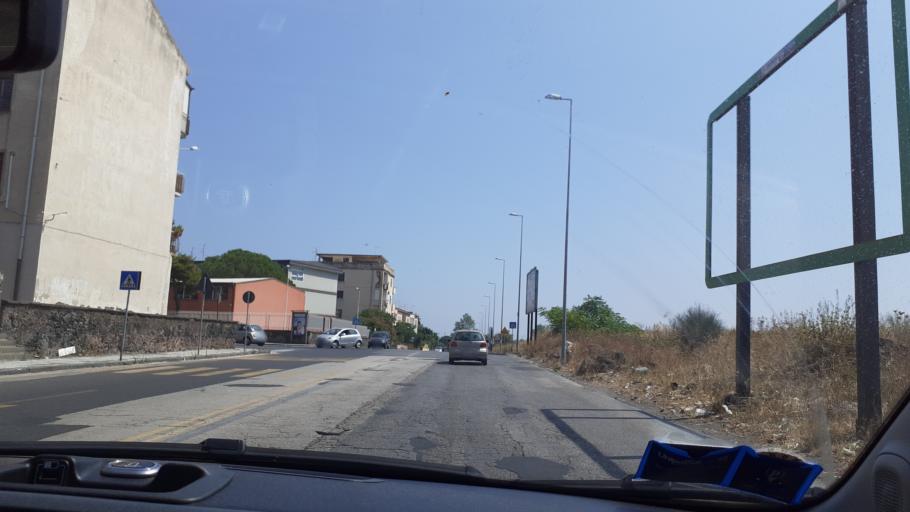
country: IT
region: Sicily
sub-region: Catania
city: Misterbianco
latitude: 37.5137
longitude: 15.0496
